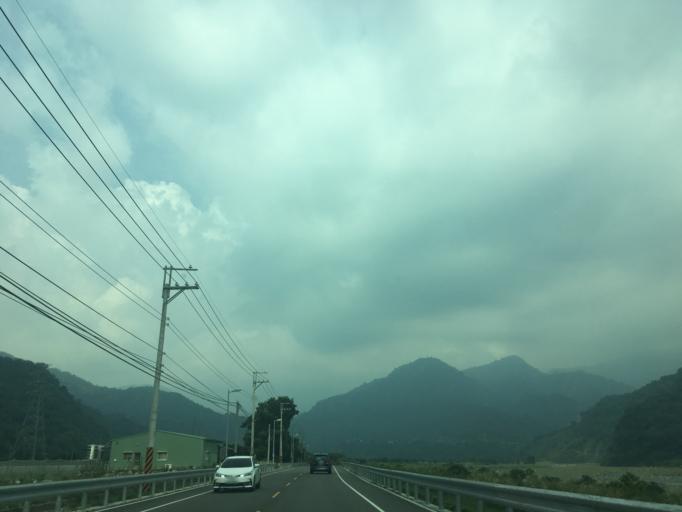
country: TW
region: Taiwan
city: Fengyuan
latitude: 24.2966
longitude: 120.8840
